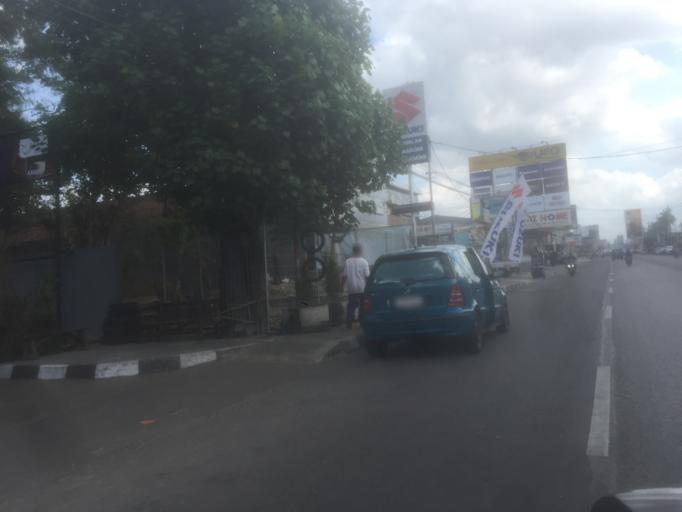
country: ID
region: Daerah Istimewa Yogyakarta
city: Yogyakarta
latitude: -7.7689
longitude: 110.3614
